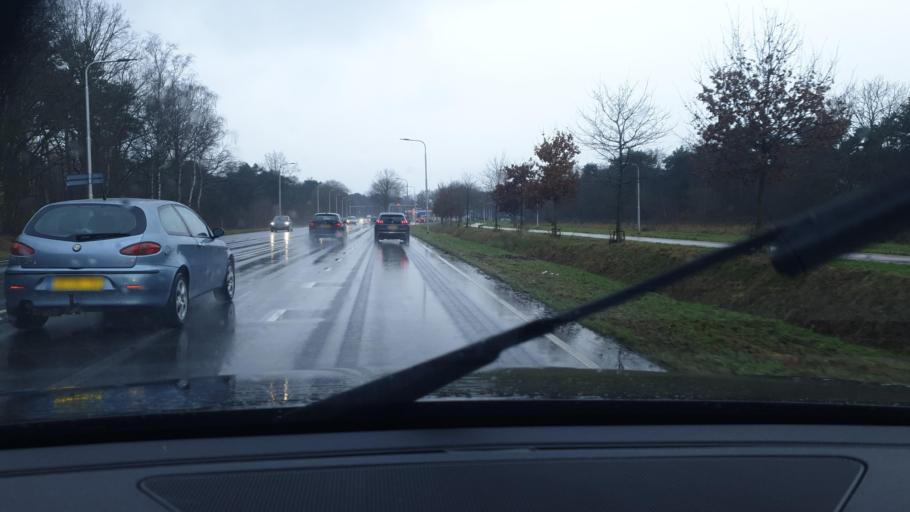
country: NL
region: North Brabant
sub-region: Gemeente Goirle
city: Goirle
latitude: 51.5774
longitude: 5.0216
